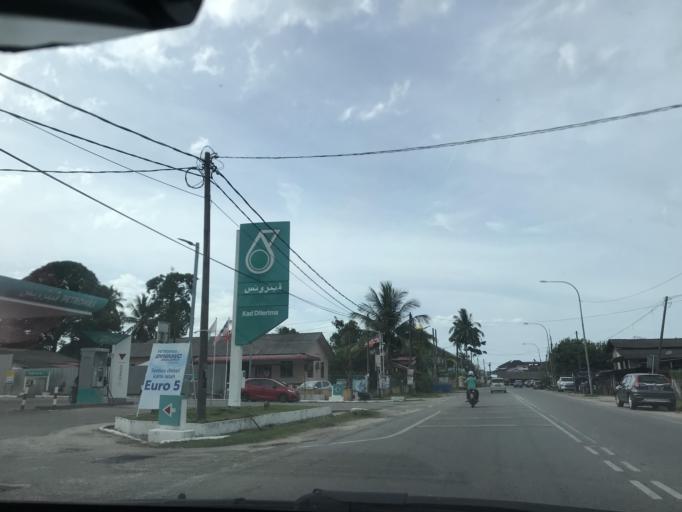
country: MY
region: Kelantan
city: Kota Bharu
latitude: 6.1011
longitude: 102.2306
